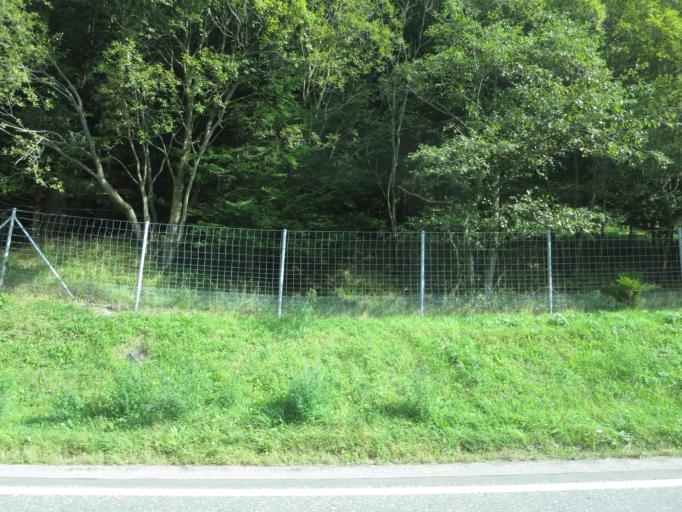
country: CH
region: Grisons
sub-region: Moesa District
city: Mesocco
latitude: 46.4221
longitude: 9.2297
